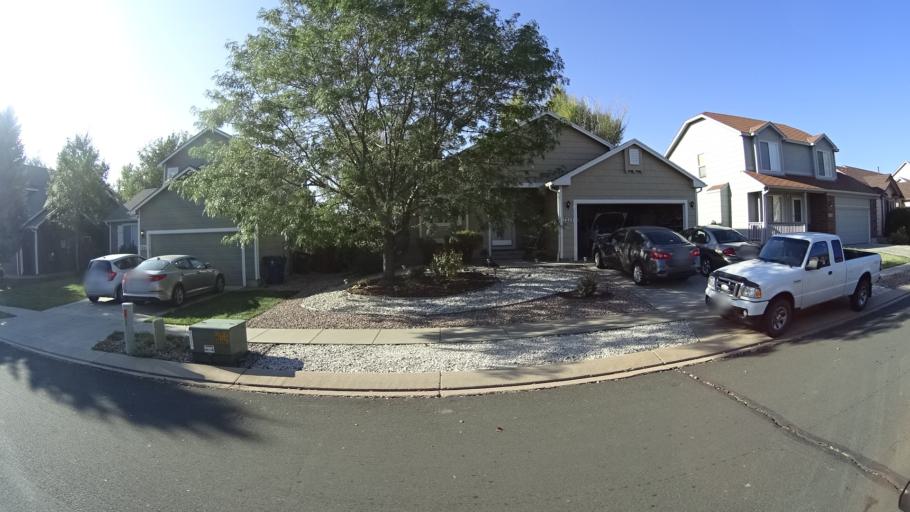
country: US
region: Colorado
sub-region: El Paso County
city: Cimarron Hills
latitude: 38.8914
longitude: -104.6921
